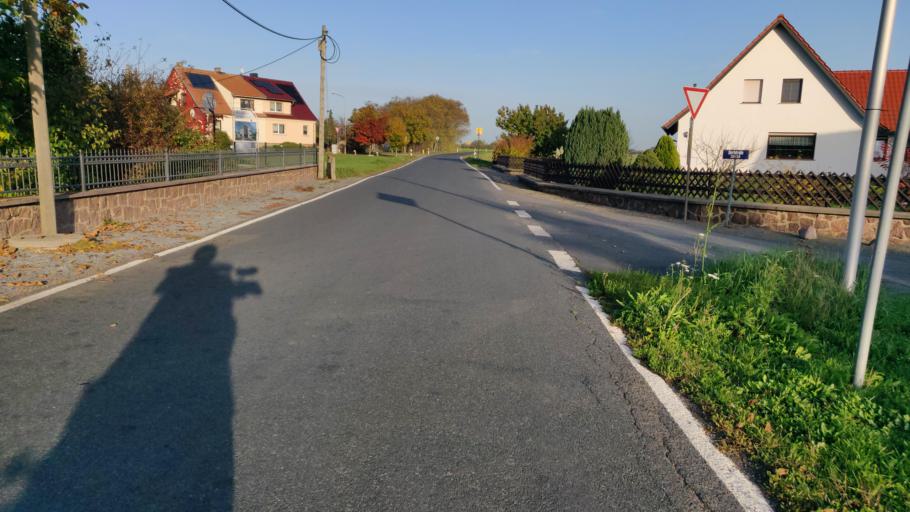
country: DE
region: Saxony
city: Grossenhain
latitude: 51.3397
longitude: 13.5637
